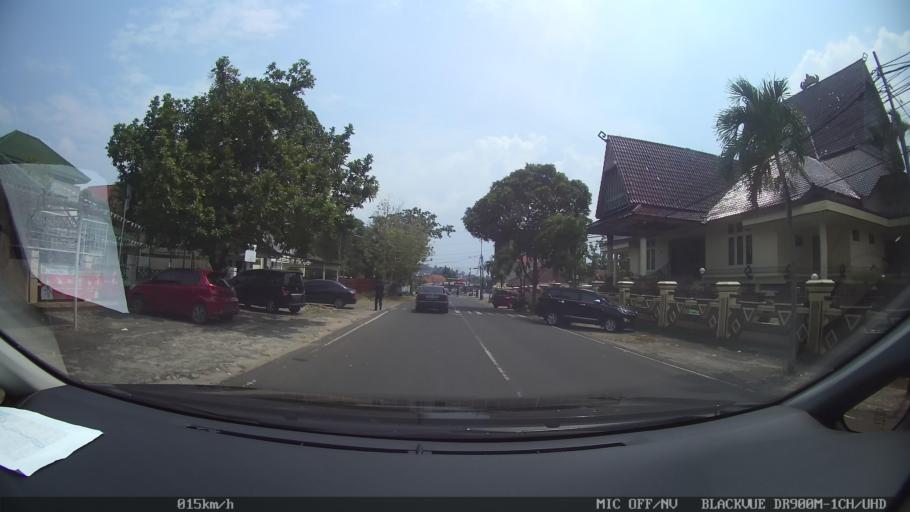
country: ID
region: Lampung
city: Bandarlampung
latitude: -5.4247
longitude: 105.2719
